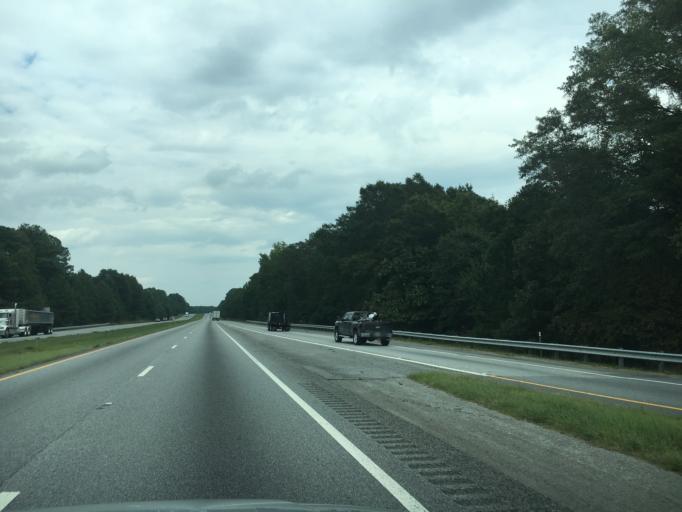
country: US
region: Georgia
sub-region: Hart County
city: Reed Creek
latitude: 34.5067
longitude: -82.9613
